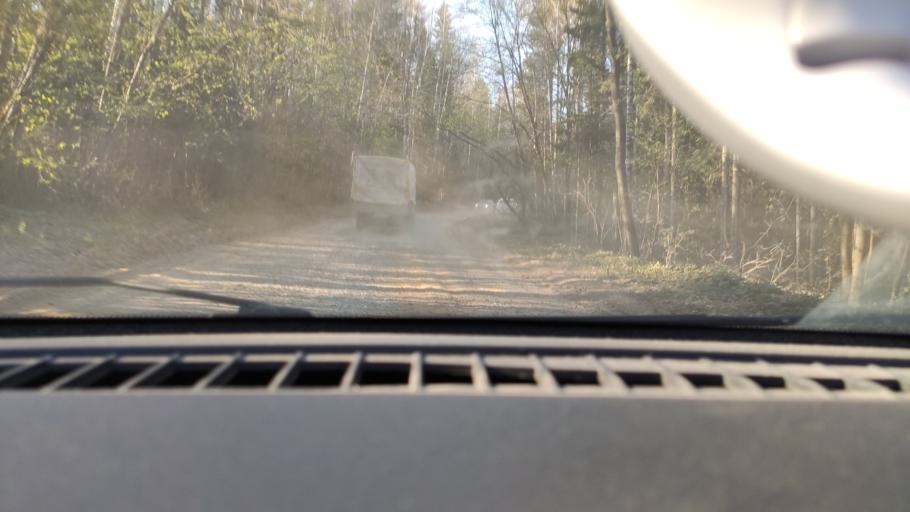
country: RU
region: Perm
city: Novyye Lyady
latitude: 58.1230
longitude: 56.4577
